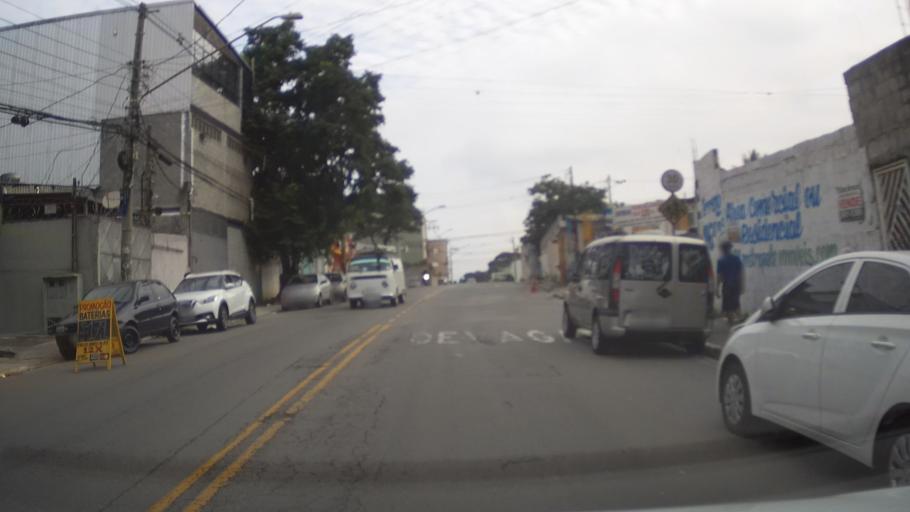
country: BR
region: Sao Paulo
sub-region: Guarulhos
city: Guarulhos
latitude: -23.4339
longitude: -46.5087
